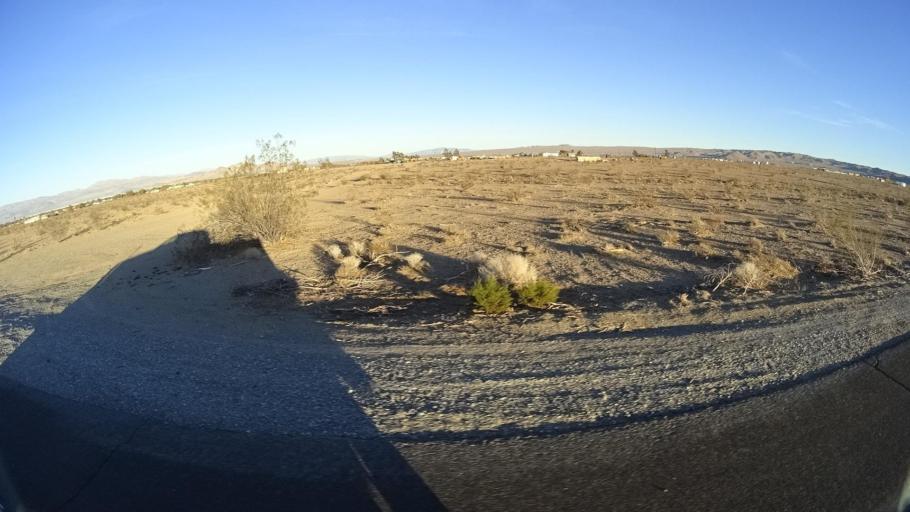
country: US
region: California
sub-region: Kern County
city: China Lake Acres
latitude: 35.6150
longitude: -117.7230
